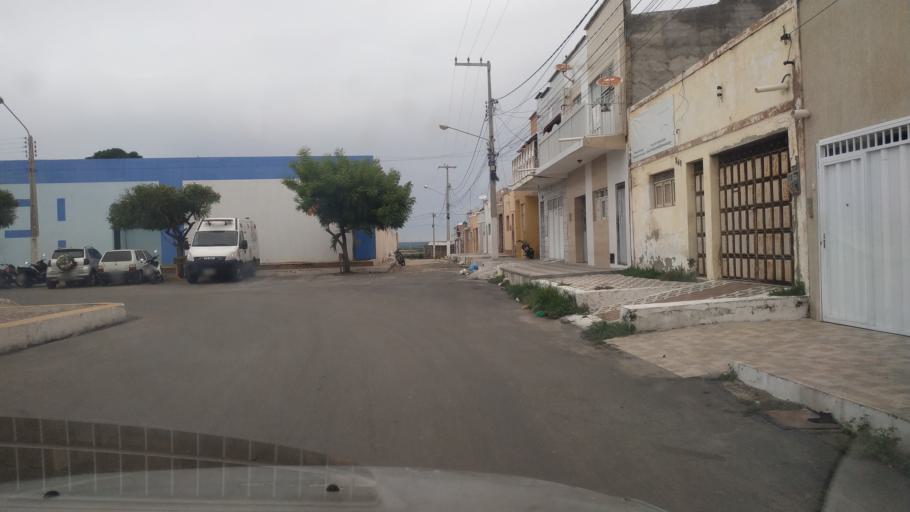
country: BR
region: Rio Grande do Norte
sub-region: Areia Branca
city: Areia Branca
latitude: -4.9579
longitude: -37.1325
